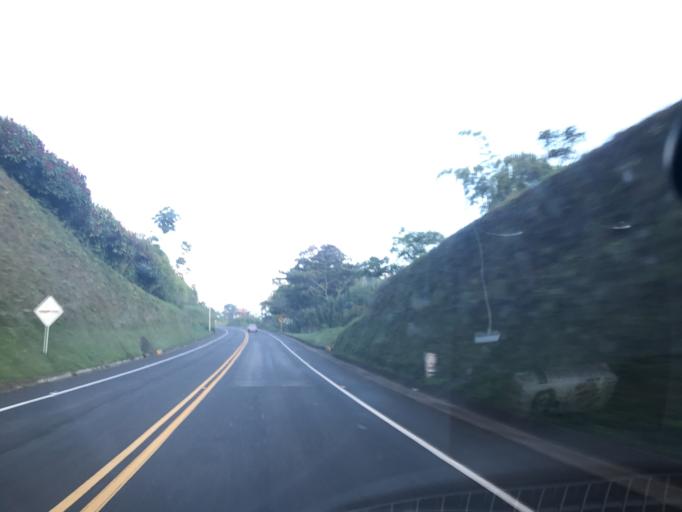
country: CO
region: Risaralda
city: Pereira
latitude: 4.7469
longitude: -75.6801
